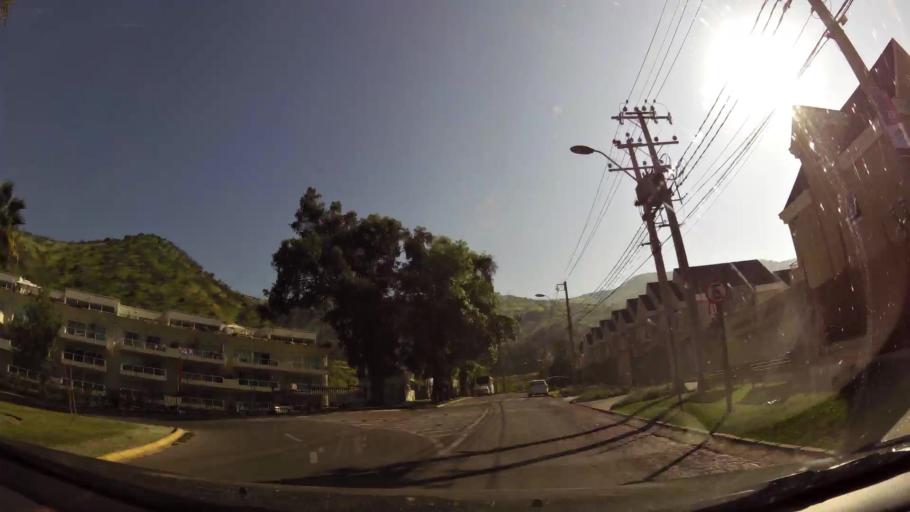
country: CL
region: Santiago Metropolitan
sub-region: Provincia de Chacabuco
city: Chicureo Abajo
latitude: -33.3390
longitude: -70.6677
